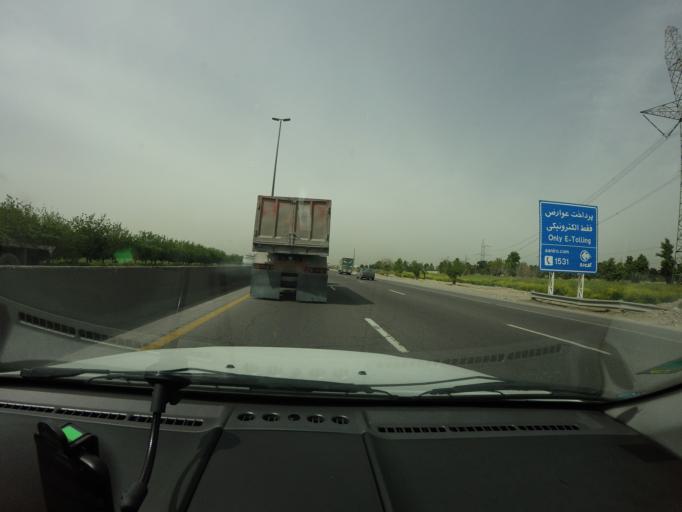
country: IR
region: Tehran
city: Eslamshahr
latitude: 35.6173
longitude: 51.2178
